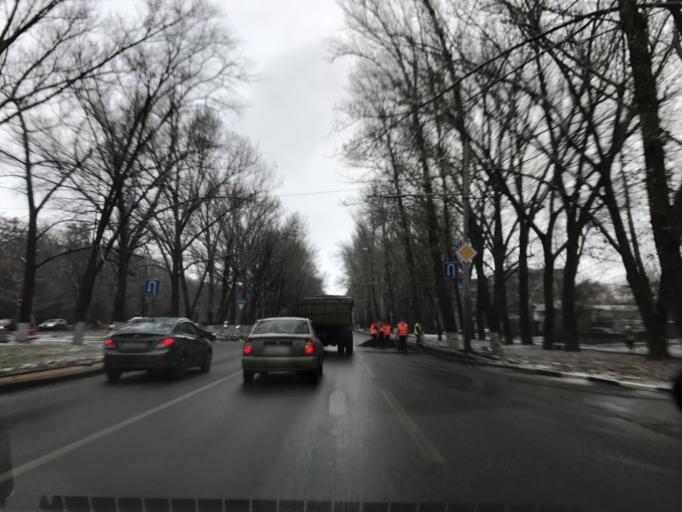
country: RU
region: Rostov
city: Aksay
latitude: 47.2636
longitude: 39.8119
